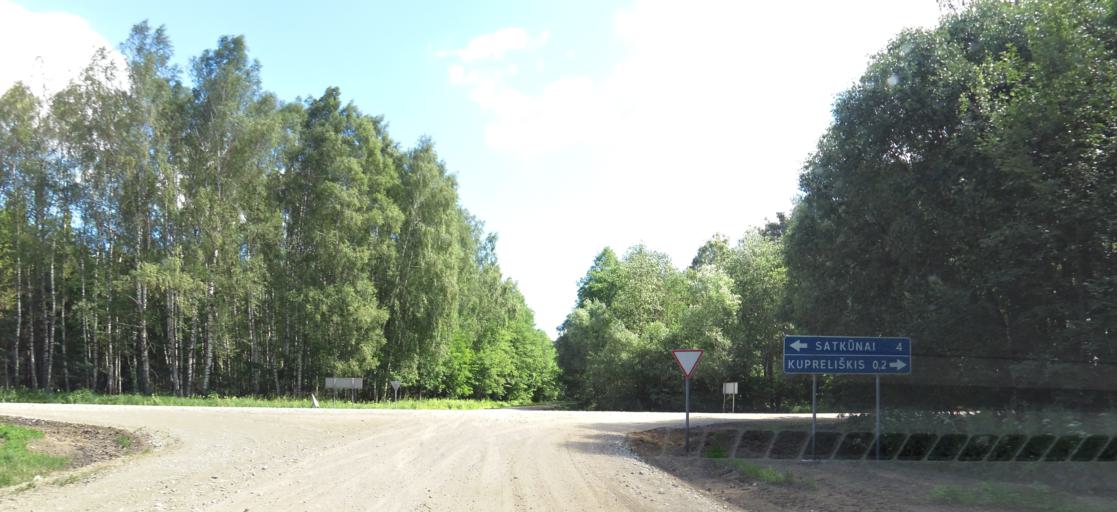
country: LT
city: Obeliai
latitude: 56.0441
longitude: 24.9594
